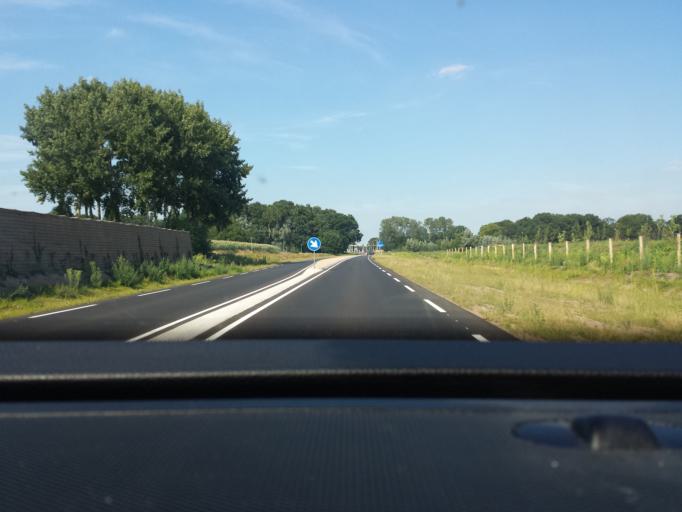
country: NL
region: Gelderland
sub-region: Gemeente Doetinchem
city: Doetinchem
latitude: 51.9638
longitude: 6.3138
